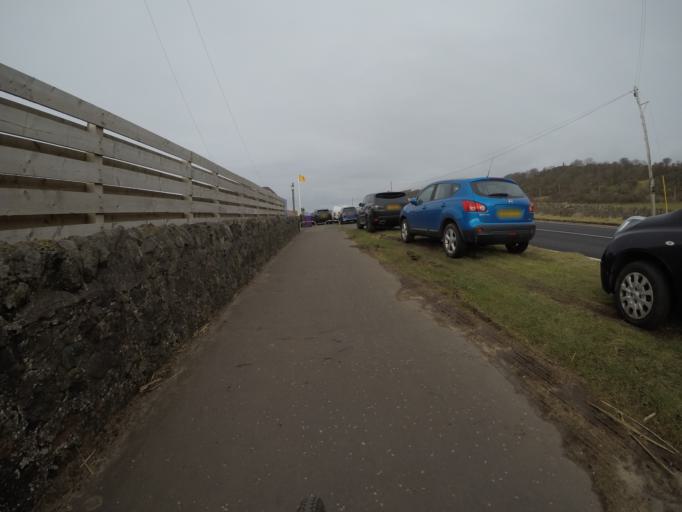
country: GB
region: Scotland
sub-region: North Ayrshire
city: West Kilbride
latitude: 55.6647
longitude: -4.8368
